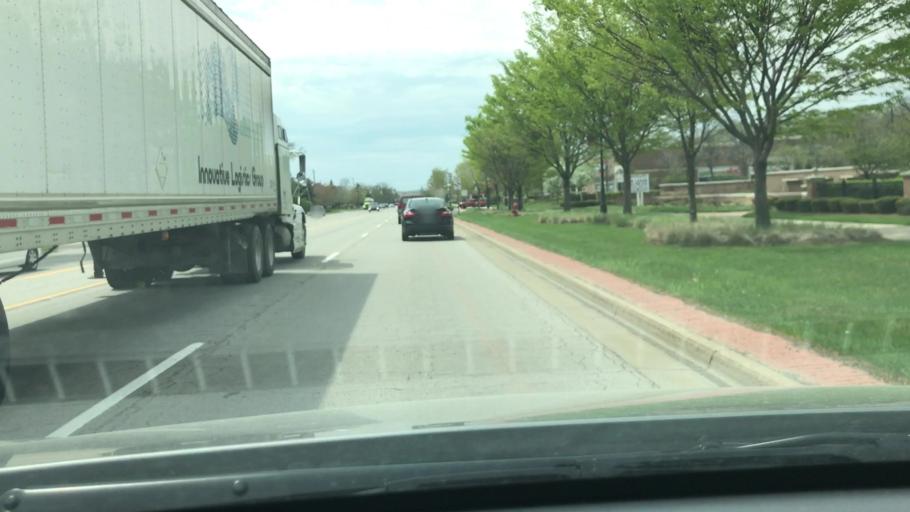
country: US
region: Michigan
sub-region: Wayne County
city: Plymouth
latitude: 42.3593
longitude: -83.4474
